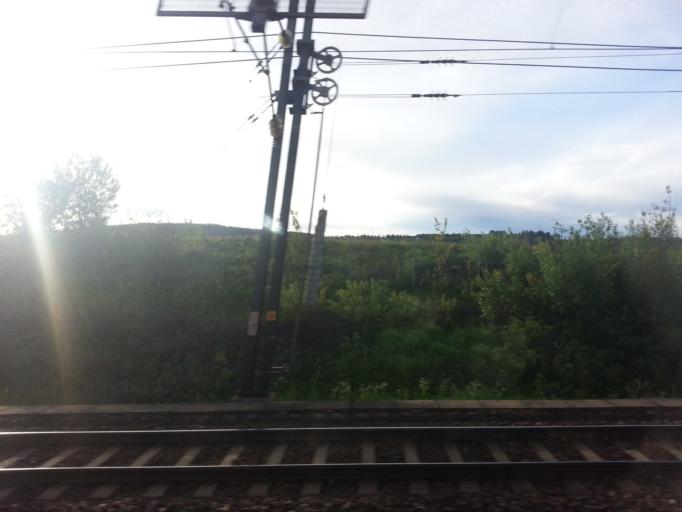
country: NO
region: Akershus
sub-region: Skedsmo
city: Leirsund
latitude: 59.9920
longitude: 11.0801
